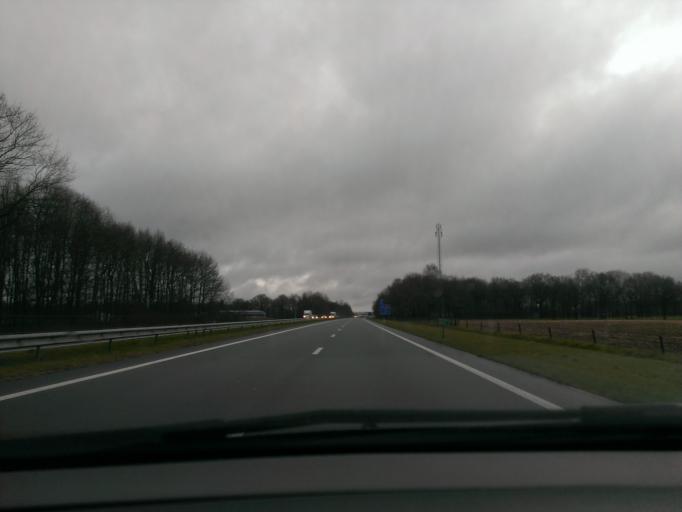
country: NL
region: Drenthe
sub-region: Gemeente Coevorden
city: Sleen
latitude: 52.7405
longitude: 6.8085
